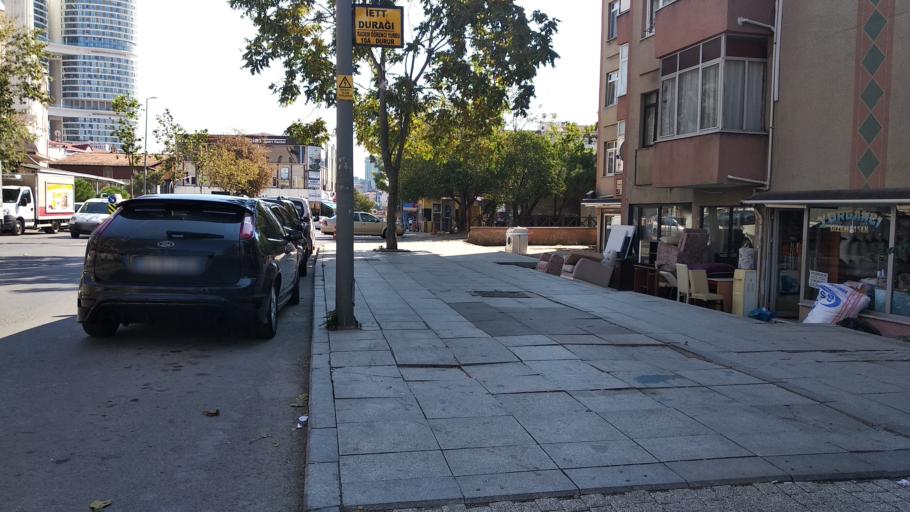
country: TR
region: Istanbul
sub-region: Atasehir
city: Atasehir
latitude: 40.9963
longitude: 29.0827
